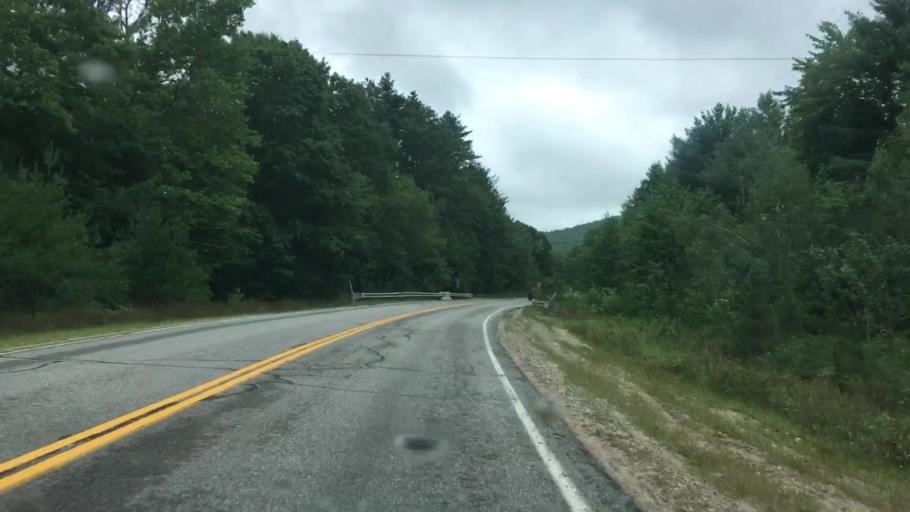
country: US
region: Maine
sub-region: Oxford County
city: Brownfield
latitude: 43.9790
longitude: -70.9269
